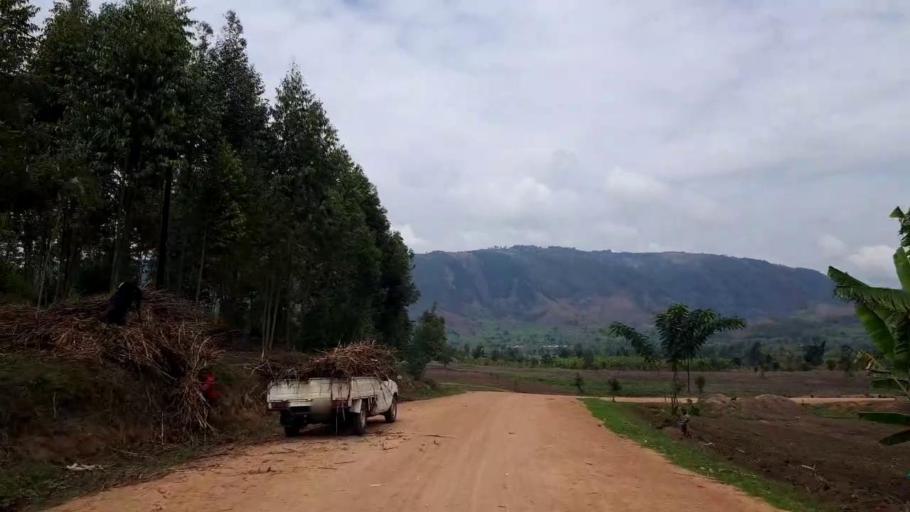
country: RW
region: Northern Province
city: Byumba
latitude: -1.5000
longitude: 30.2084
